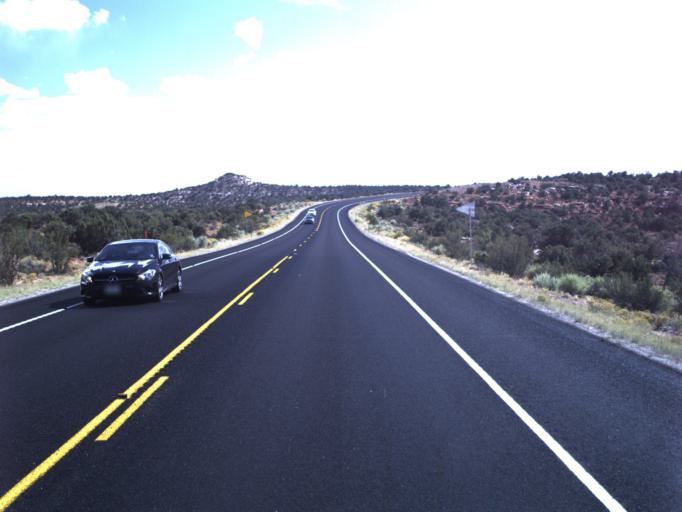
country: US
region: Utah
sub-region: Grand County
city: Moab
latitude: 38.5703
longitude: -109.7919
